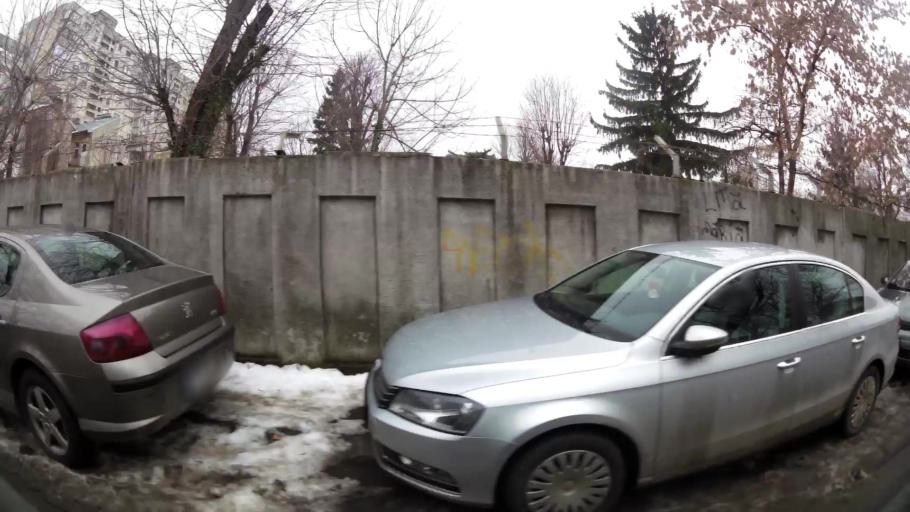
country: RO
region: Bucuresti
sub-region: Municipiul Bucuresti
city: Bucuresti
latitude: 44.4585
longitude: 26.0642
